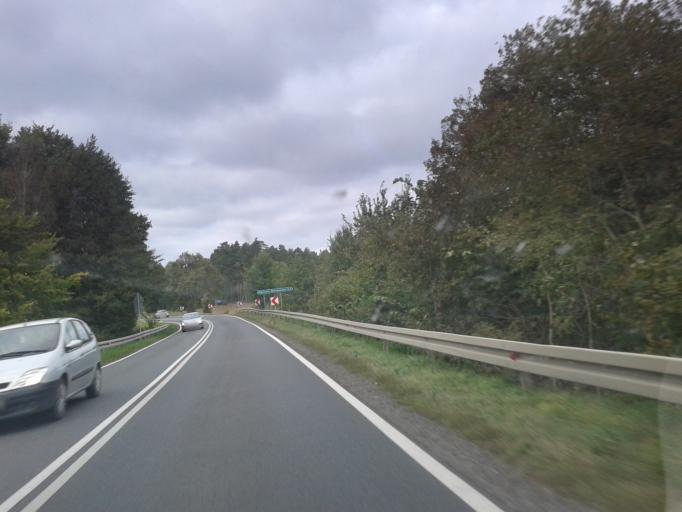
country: PL
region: Kujawsko-Pomorskie
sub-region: Powiat sepolenski
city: Sepolno Krajenskie
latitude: 53.4690
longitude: 17.5273
